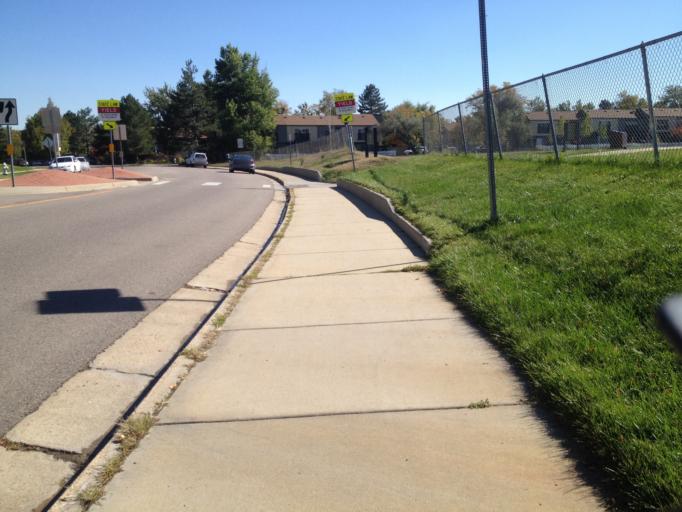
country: US
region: Colorado
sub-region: Boulder County
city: Boulder
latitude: 39.9834
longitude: -105.2391
